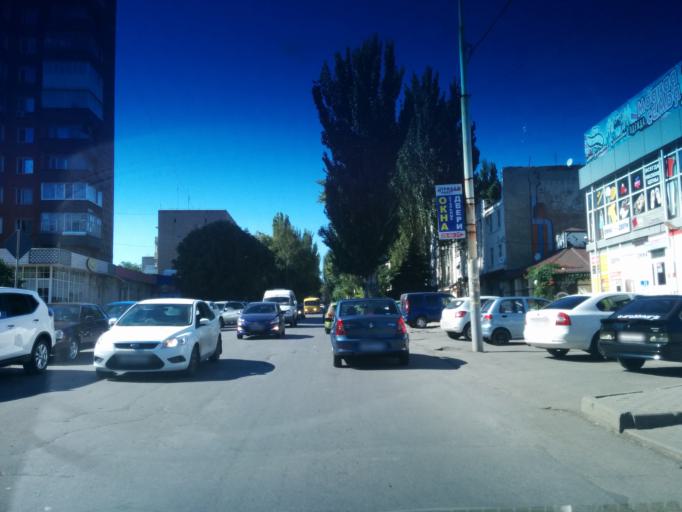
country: RU
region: Rostov
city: Shakhty
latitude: 47.7110
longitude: 40.2160
